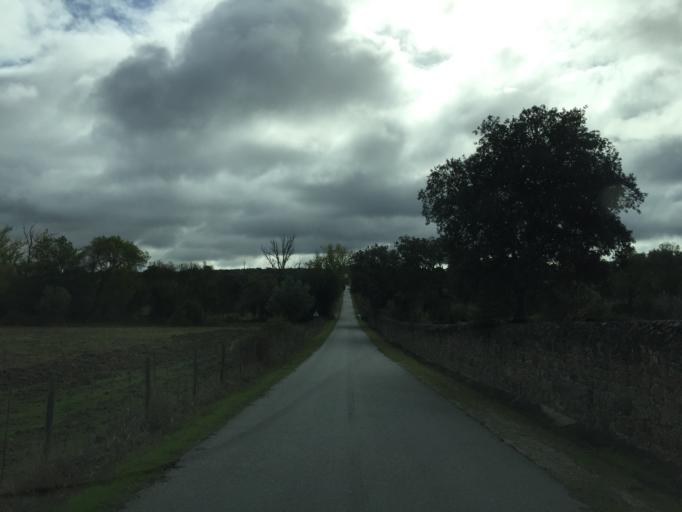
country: PT
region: Portalegre
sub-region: Alter do Chao
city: Alter do Chao
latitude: 39.2309
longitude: -7.6842
